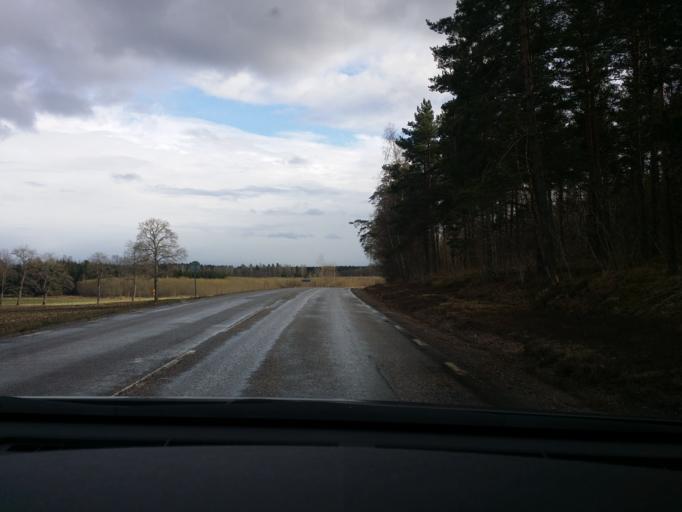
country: SE
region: Soedermanland
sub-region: Eskilstuna Kommun
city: Arla
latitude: 59.3084
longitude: 16.6831
